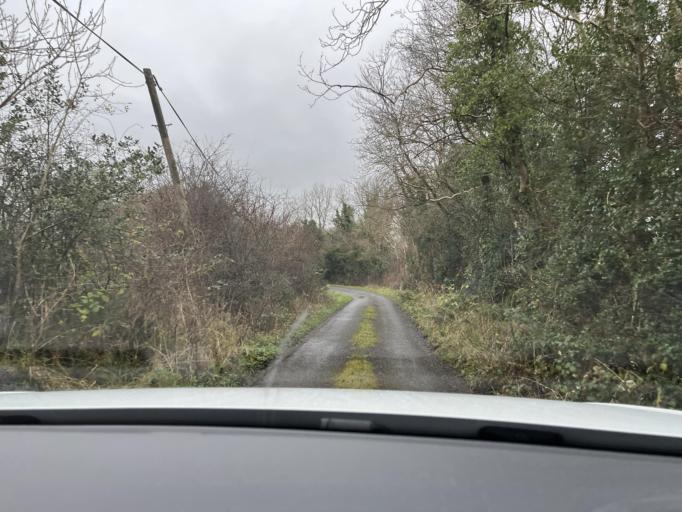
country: IE
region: Connaught
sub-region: County Leitrim
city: Manorhamilton
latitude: 54.2874
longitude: -8.1212
